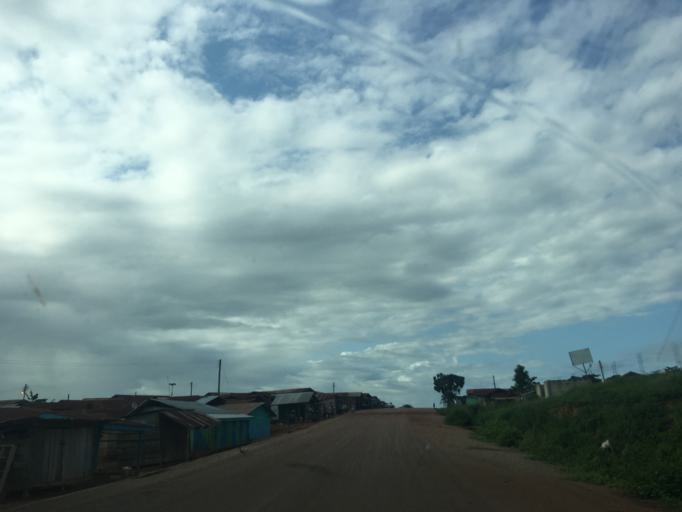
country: GH
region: Western
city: Wassa-Akropong
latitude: 6.0019
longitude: -2.4104
